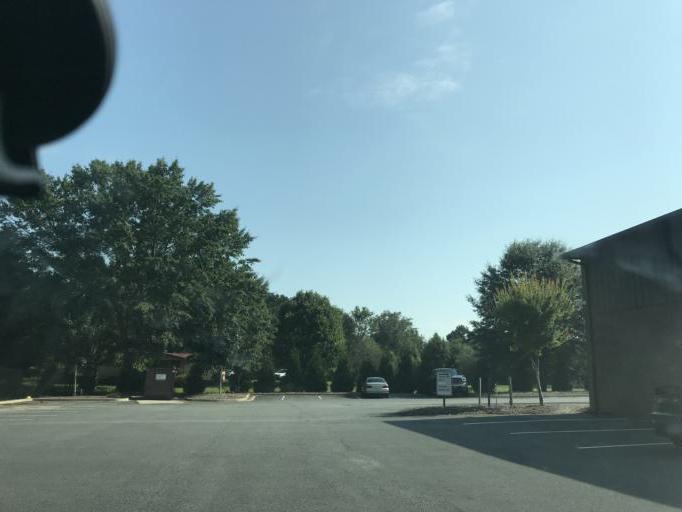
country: US
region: Georgia
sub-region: Forsyth County
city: Cumming
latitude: 34.2612
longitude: -84.1069
